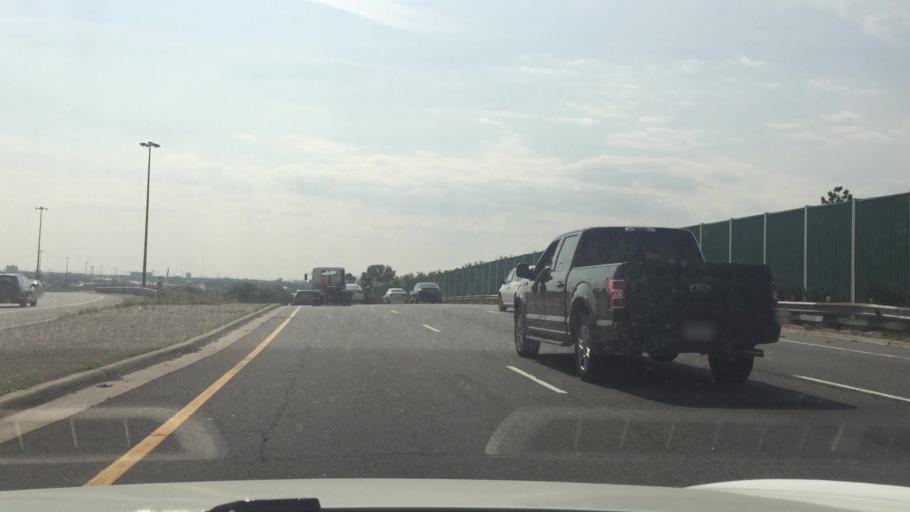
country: CA
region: Ontario
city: Concord
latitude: 43.7203
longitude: -79.4962
